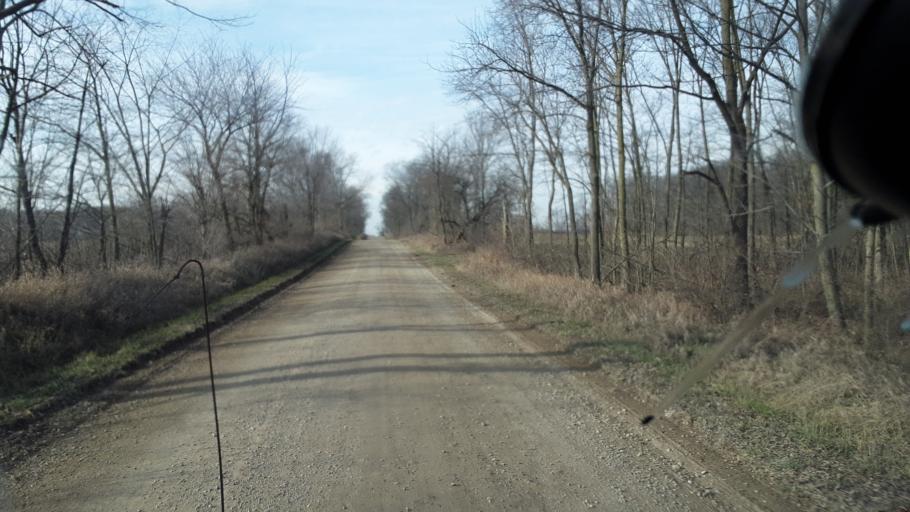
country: US
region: Ohio
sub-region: Defiance County
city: Hicksville
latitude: 41.2699
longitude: -84.8529
